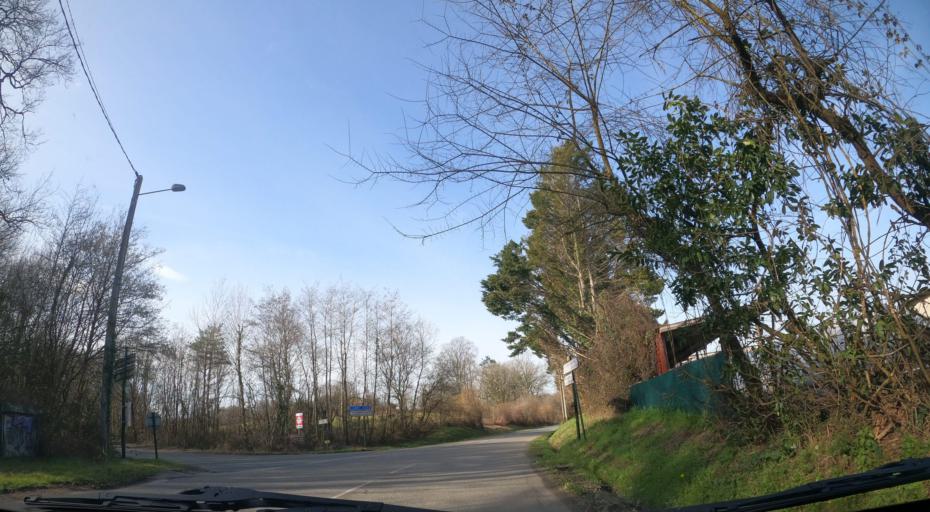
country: FR
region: Aquitaine
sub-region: Departement des Pyrenees-Atlantiques
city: Lahonce
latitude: 43.4520
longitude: -1.3793
